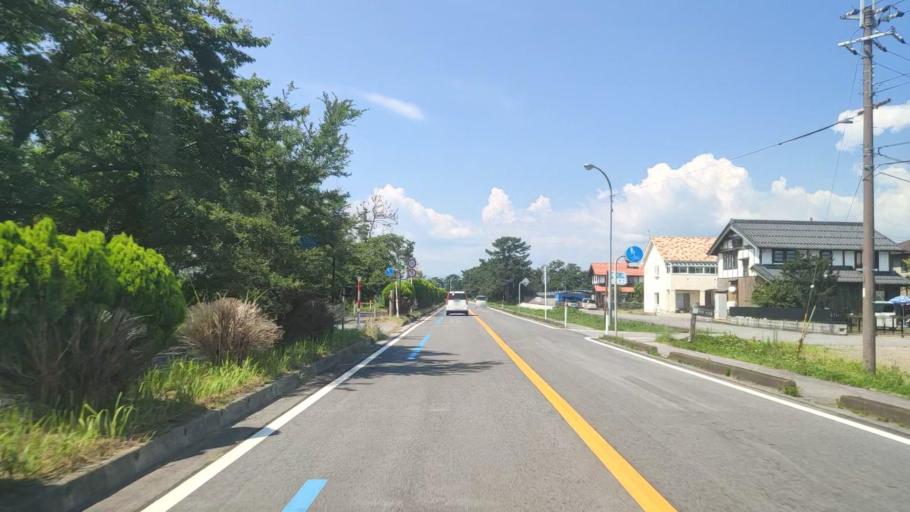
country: JP
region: Shiga Prefecture
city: Nagahama
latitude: 35.3937
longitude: 136.2176
